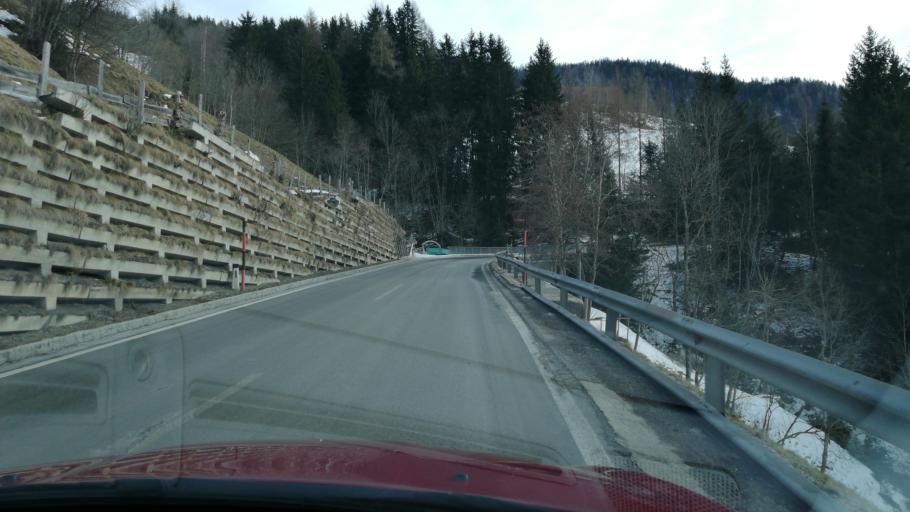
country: AT
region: Styria
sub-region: Politischer Bezirk Liezen
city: Donnersbach
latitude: 47.4525
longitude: 14.1419
